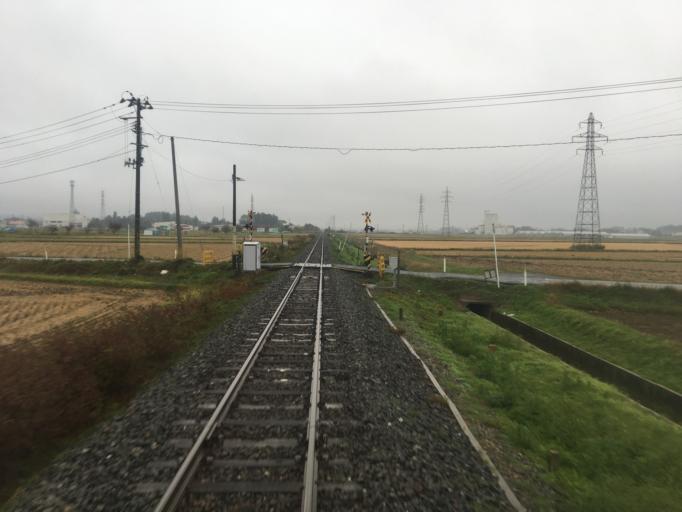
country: JP
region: Miyagi
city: Kogota
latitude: 38.5561
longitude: 141.0378
